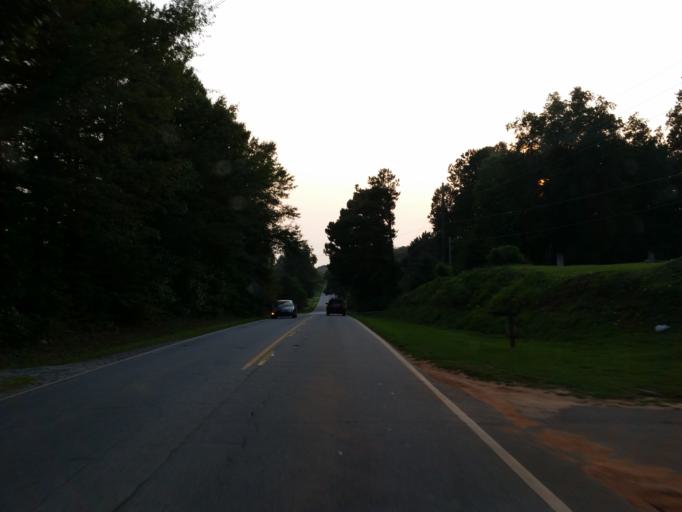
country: US
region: Georgia
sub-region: Spalding County
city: East Griffin
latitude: 33.2899
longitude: -84.1763
